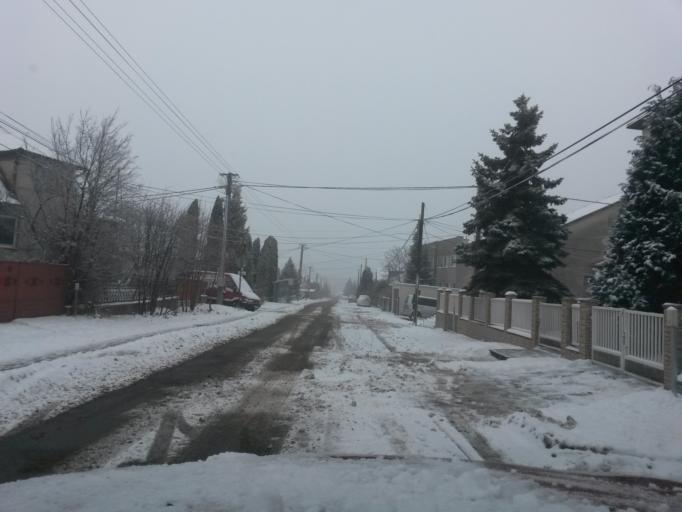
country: SK
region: Kosicky
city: Kosice
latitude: 48.7313
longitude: 21.3008
